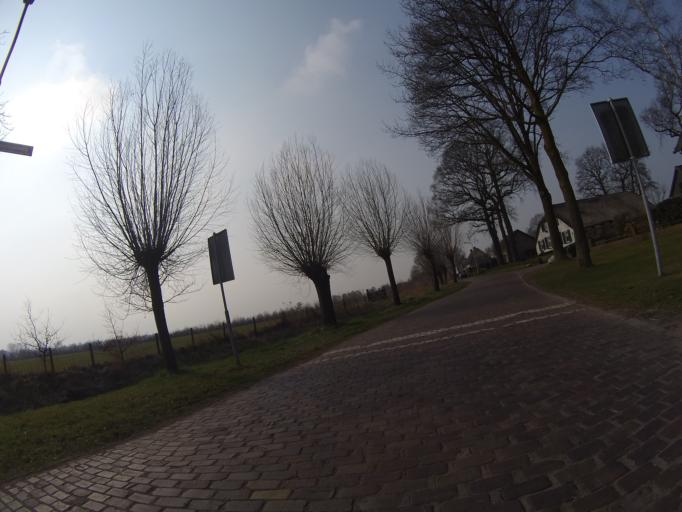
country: NL
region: Utrecht
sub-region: Gemeente Amersfoort
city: Hoogland
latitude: 52.1995
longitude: 5.3653
